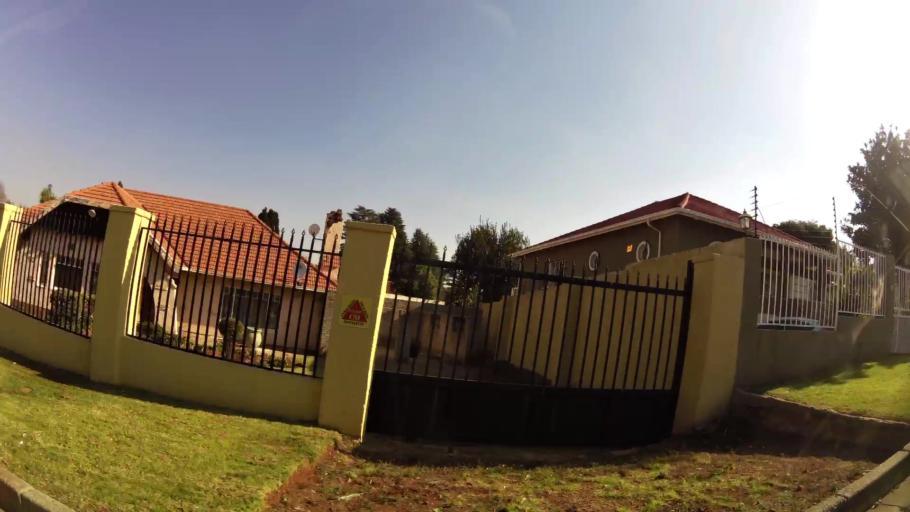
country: ZA
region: Gauteng
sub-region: City of Johannesburg Metropolitan Municipality
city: Johannesburg
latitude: -26.1741
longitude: 28.1067
